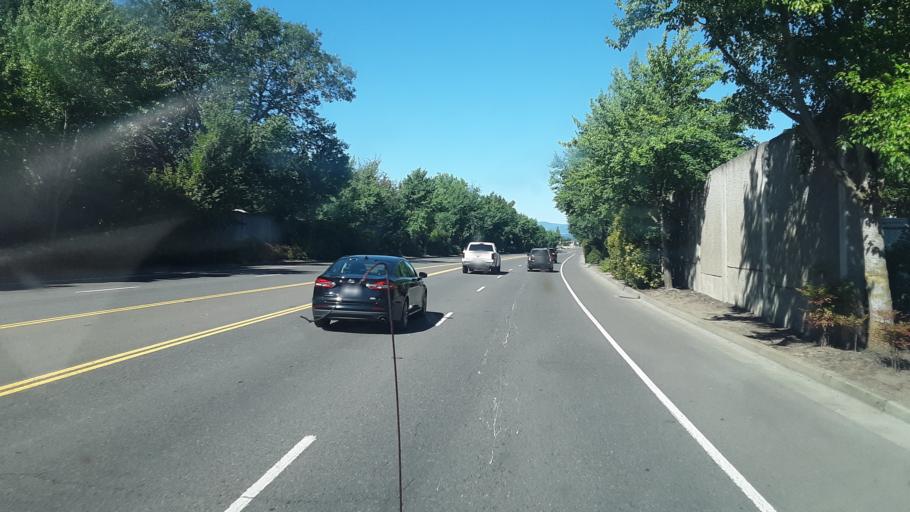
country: US
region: Oregon
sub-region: Josephine County
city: Fruitdale
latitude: 42.4269
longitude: -123.3210
